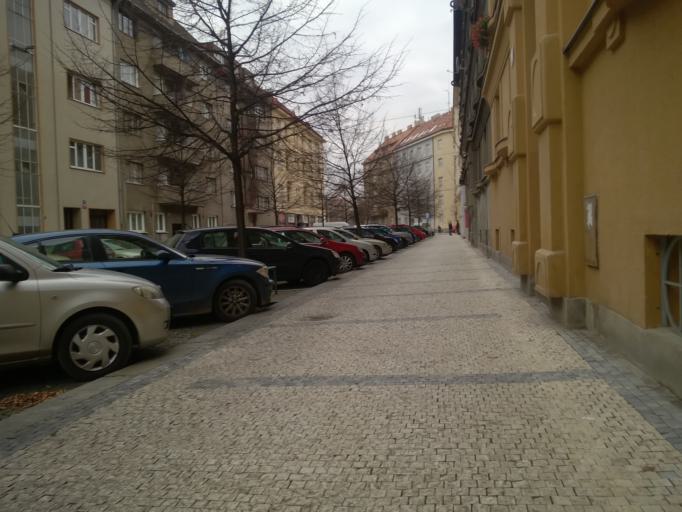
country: CZ
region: Praha
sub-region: Praha 1
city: Mala Strana
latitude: 50.1024
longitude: 14.3986
